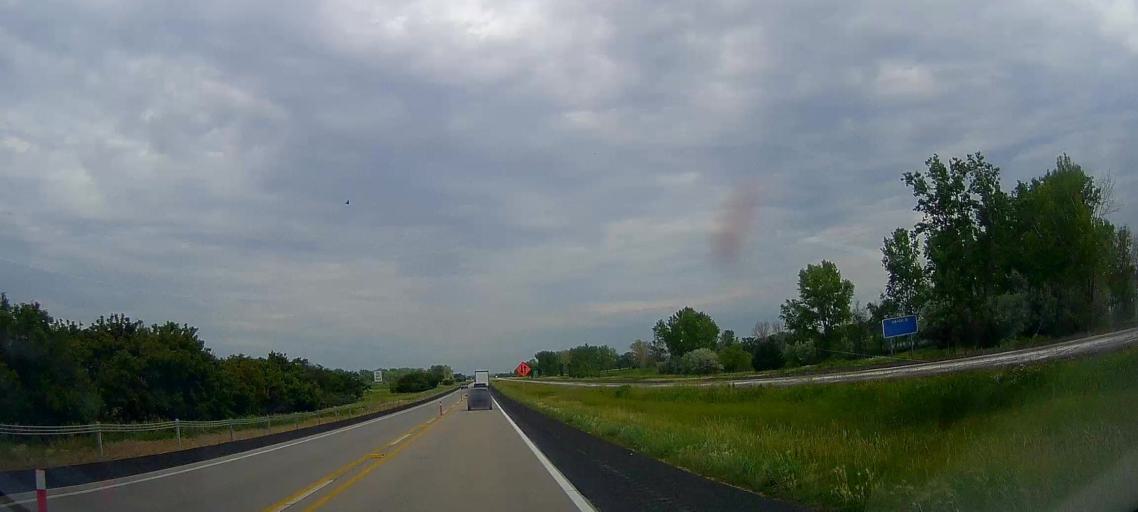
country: US
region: Iowa
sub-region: Harrison County
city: Missouri Valley
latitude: 41.6371
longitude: -96.0095
